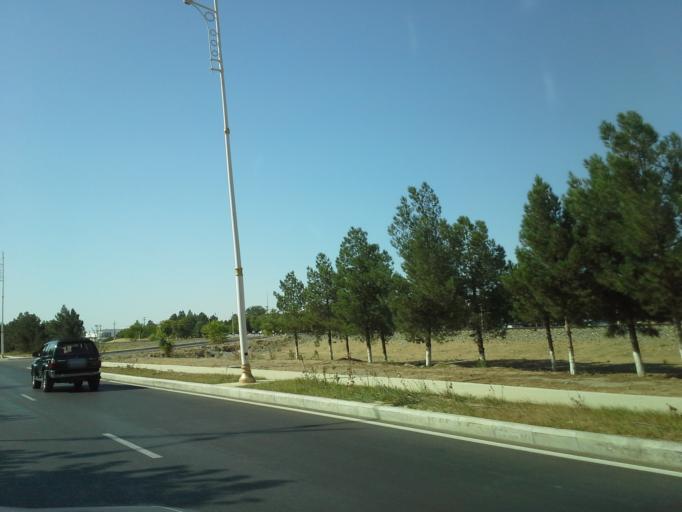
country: TM
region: Ahal
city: Ashgabat
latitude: 37.9217
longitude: 58.4442
